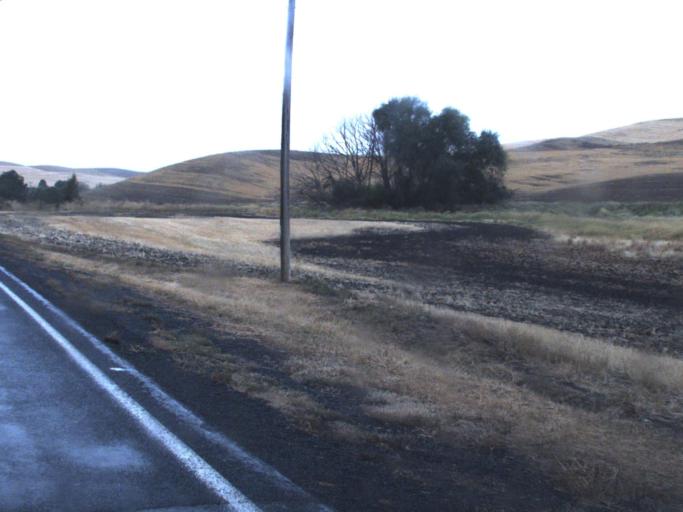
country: US
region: Washington
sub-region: Whitman County
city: Colfax
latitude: 47.0025
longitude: -117.4379
